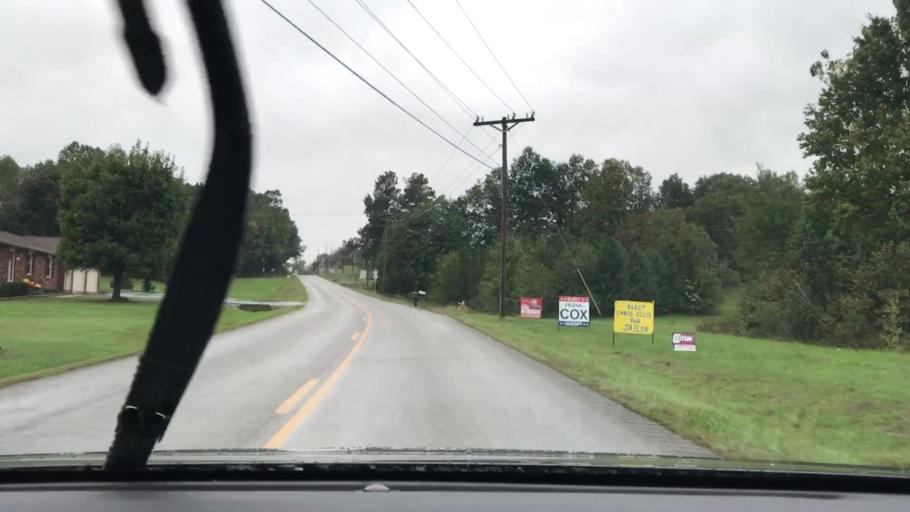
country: US
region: Kentucky
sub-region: McLean County
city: Calhoun
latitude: 37.4228
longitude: -87.2629
